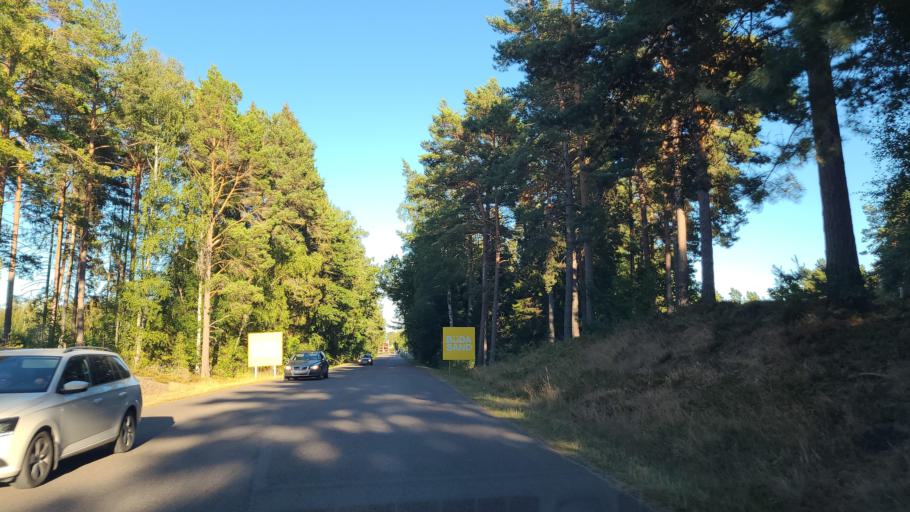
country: SE
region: Kalmar
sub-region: Borgholms Kommun
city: Borgholm
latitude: 57.2757
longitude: 17.0419
